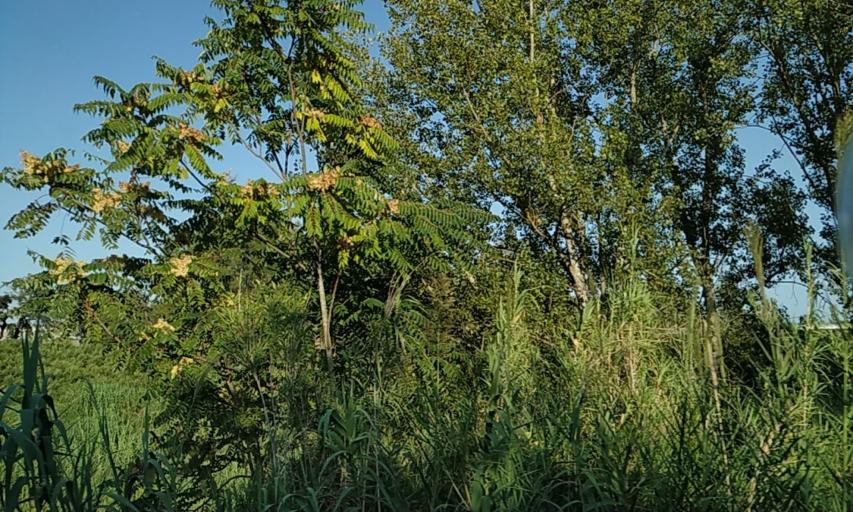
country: PT
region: Santarem
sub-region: Santarem
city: Santarem
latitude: 39.3309
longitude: -8.6593
